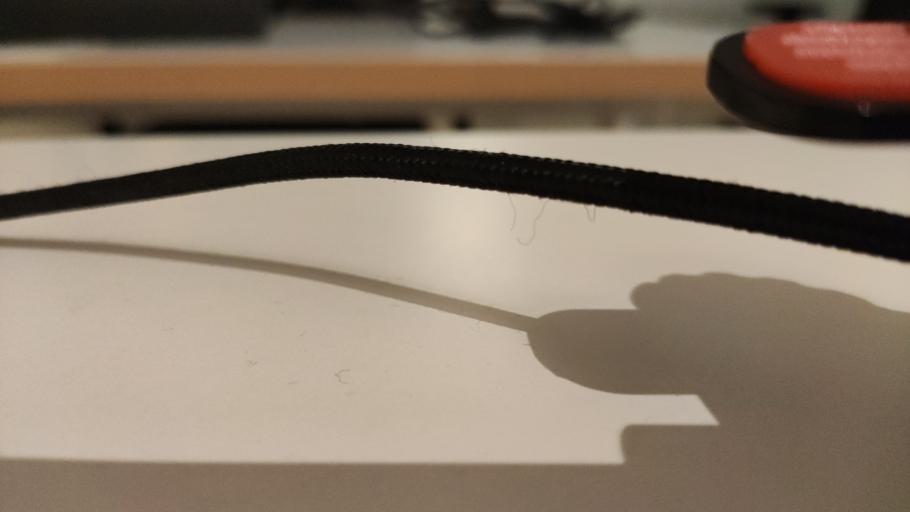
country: RU
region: Moskovskaya
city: Kurovskoye
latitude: 55.5980
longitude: 38.9248
